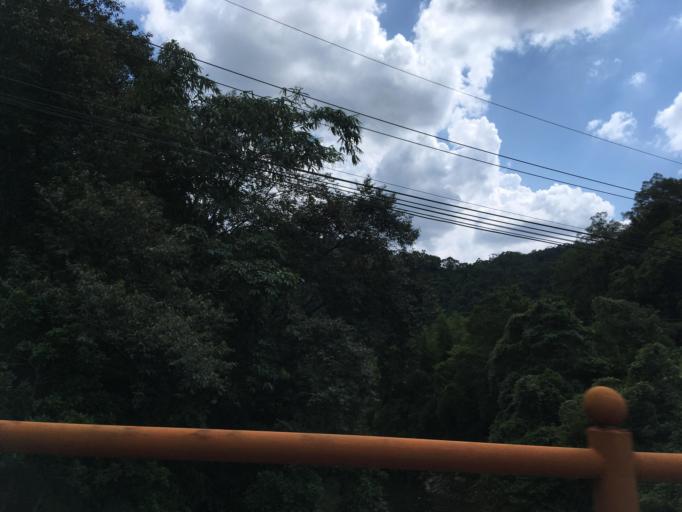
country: TW
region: Taiwan
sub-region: Yilan
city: Yilan
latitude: 24.9298
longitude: 121.6914
